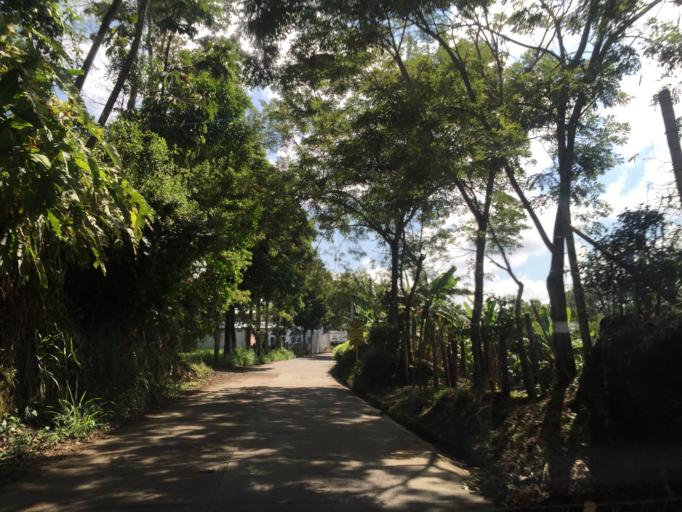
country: CO
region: Valle del Cauca
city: Ulloa
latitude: 4.6998
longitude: -75.7482
